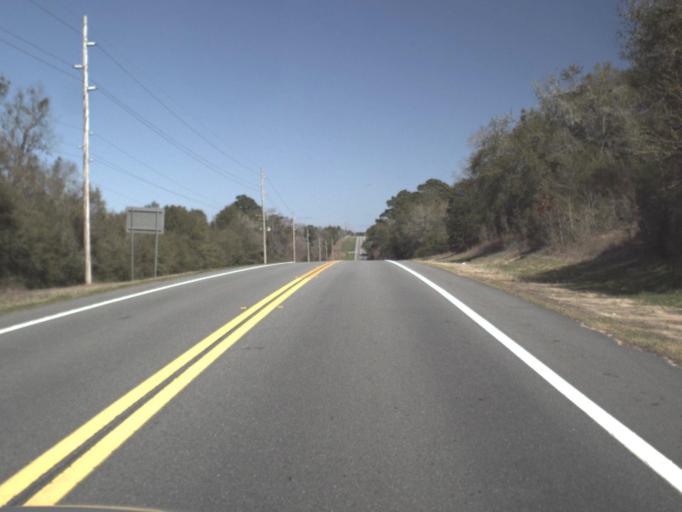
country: US
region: Florida
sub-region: Gadsden County
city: Quincy
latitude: 30.4460
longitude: -84.6445
